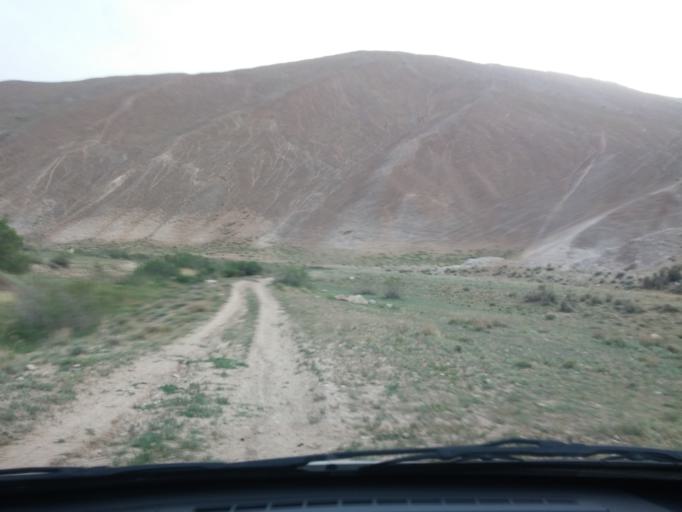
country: IR
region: Semnan
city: Istgah-e Rah Ahan-e Garmsar
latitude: 35.4734
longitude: 52.2884
